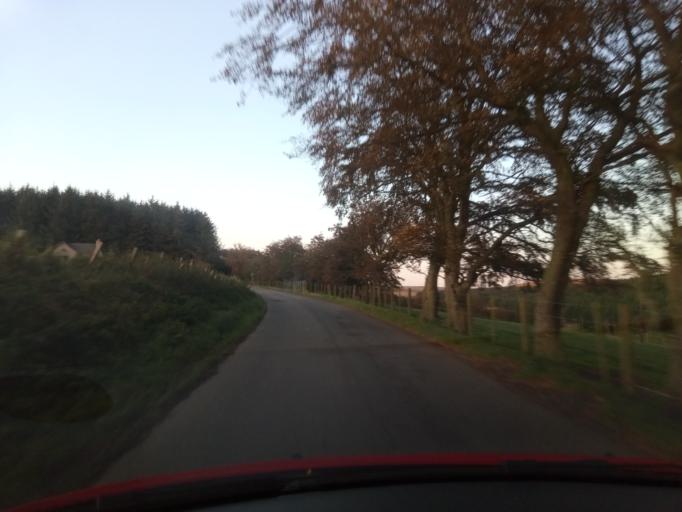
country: GB
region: Scotland
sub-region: Fife
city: Pathhead
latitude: 55.7930
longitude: -2.8899
